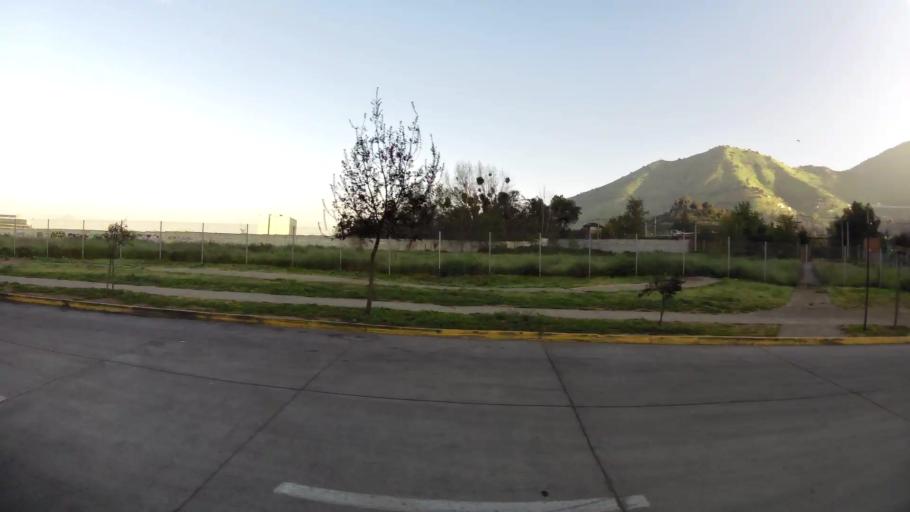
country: CL
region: Santiago Metropolitan
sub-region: Provincia de Santiago
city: Santiago
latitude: -33.3849
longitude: -70.6150
